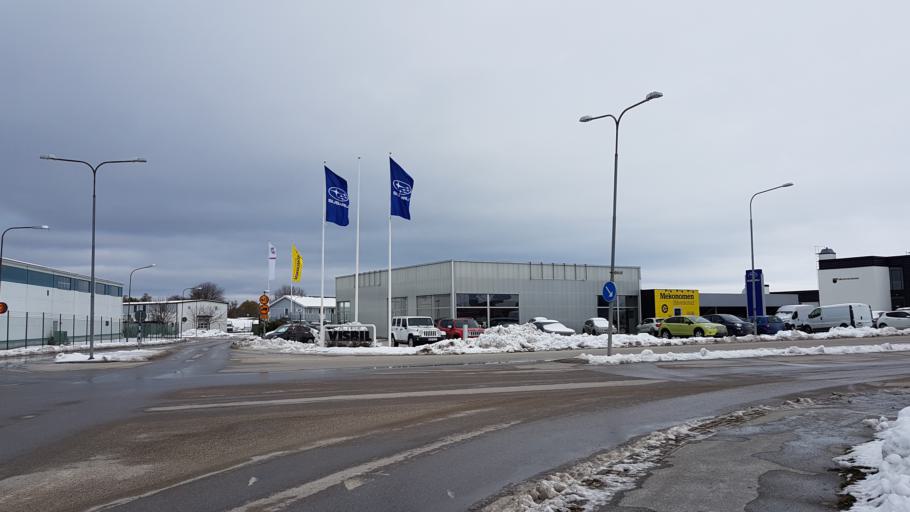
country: SE
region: Gotland
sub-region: Gotland
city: Visby
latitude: 57.6452
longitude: 18.3159
